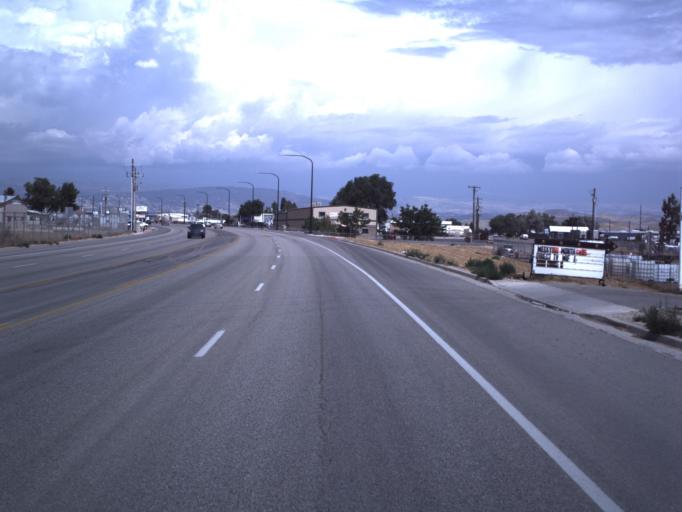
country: US
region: Utah
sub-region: Uintah County
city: Naples
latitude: 40.4446
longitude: -109.4998
